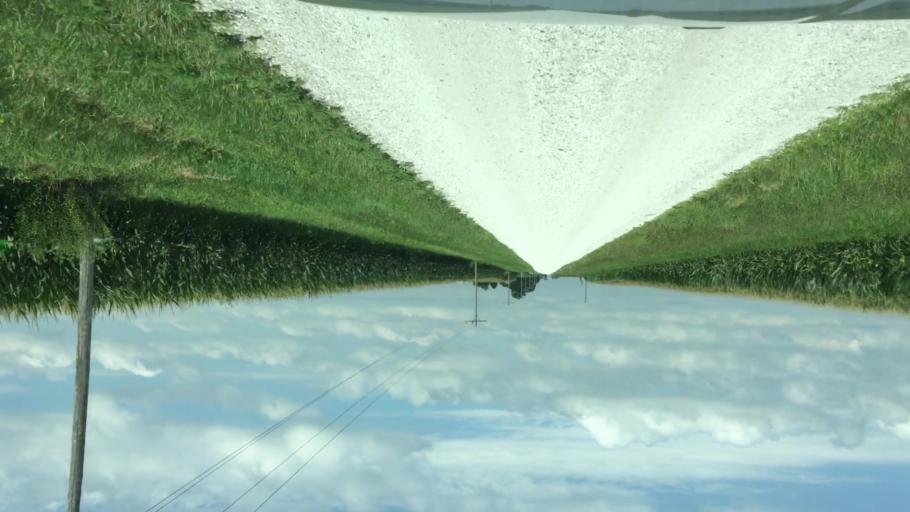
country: US
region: Illinois
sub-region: Hancock County
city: Nauvoo
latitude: 40.5218
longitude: -91.3013
